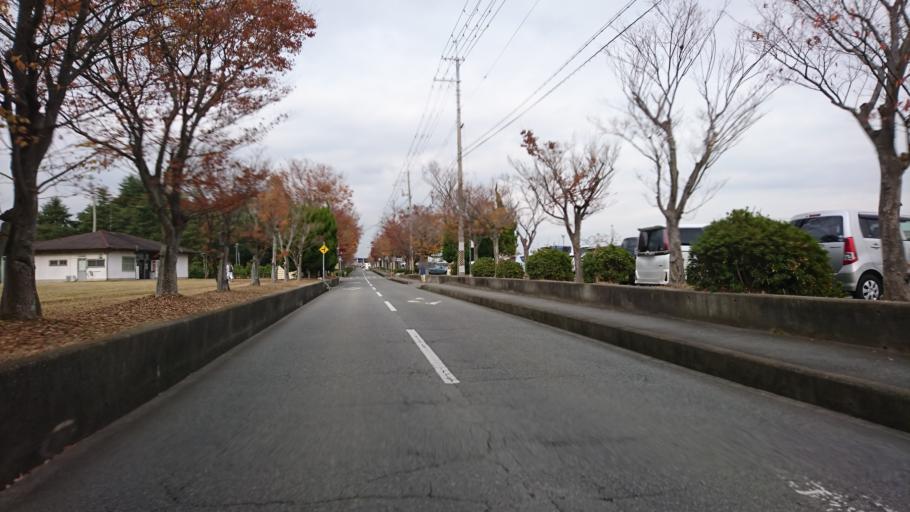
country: JP
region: Hyogo
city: Kakogawacho-honmachi
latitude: 34.7732
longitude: 134.8642
